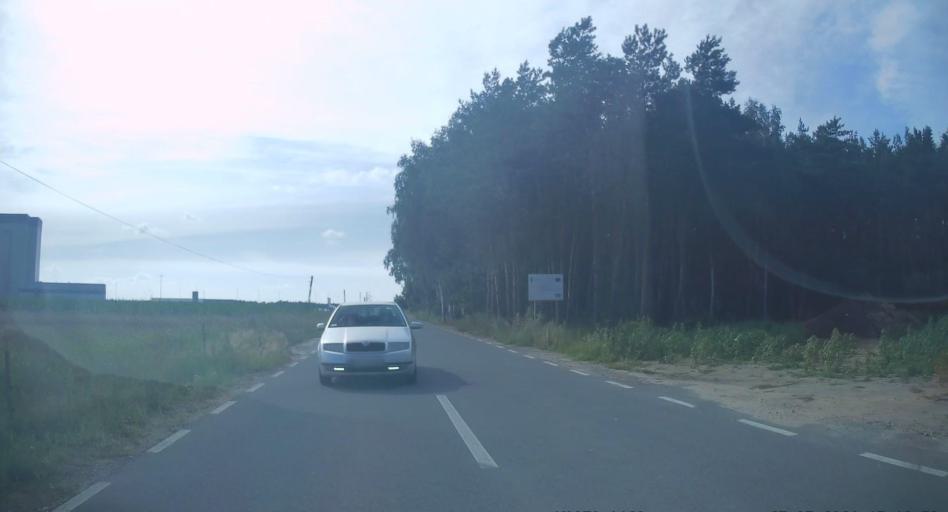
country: PL
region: Lodz Voivodeship
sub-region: Powiat rawski
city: Rawa Mazowiecka
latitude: 51.7016
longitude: 20.2313
